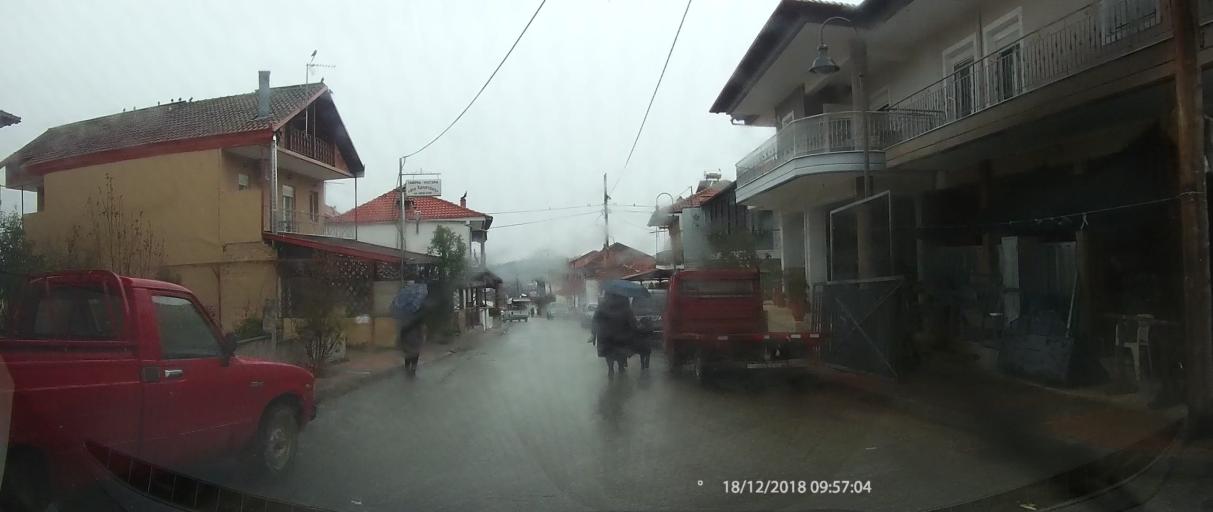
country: GR
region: Thessaly
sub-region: Nomos Larisis
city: Livadi
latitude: 40.0229
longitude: 22.2412
